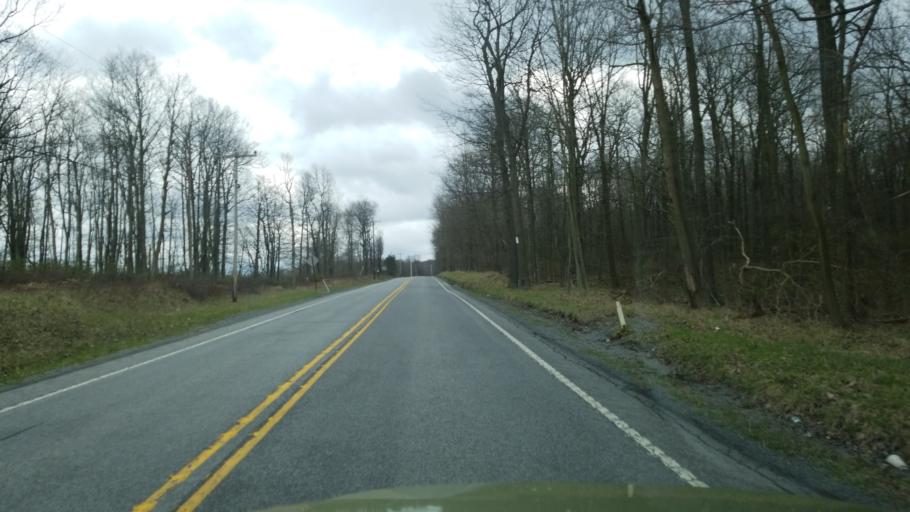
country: US
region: Pennsylvania
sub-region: Blair County
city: Tipton
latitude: 40.7328
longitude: -78.3763
